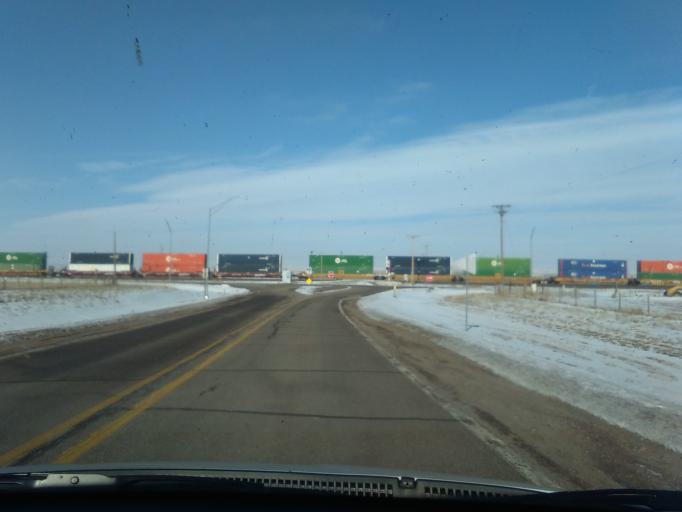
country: US
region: Wyoming
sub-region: Laramie County
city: Pine Bluffs
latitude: 41.1859
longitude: -104.0455
